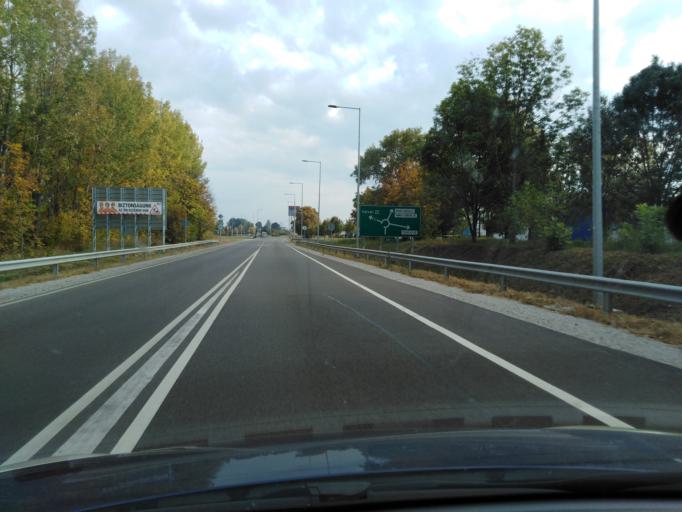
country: HU
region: Heves
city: Hatvan
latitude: 47.6800
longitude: 19.6668
